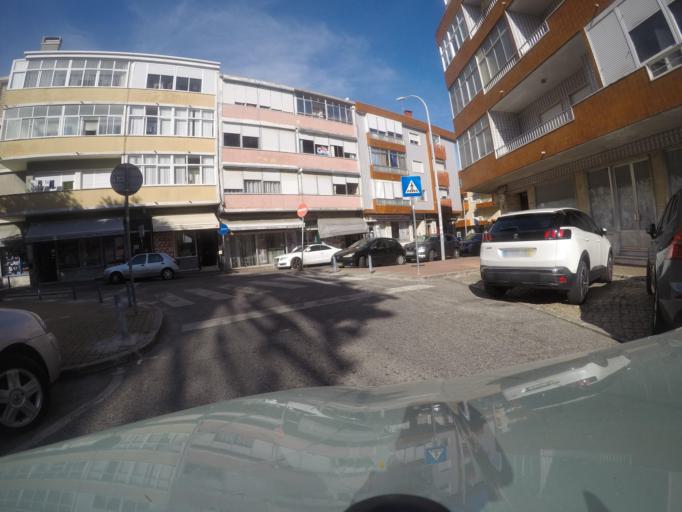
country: PT
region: Lisbon
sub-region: Amadora
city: Amadora
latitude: 38.7582
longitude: -9.2393
